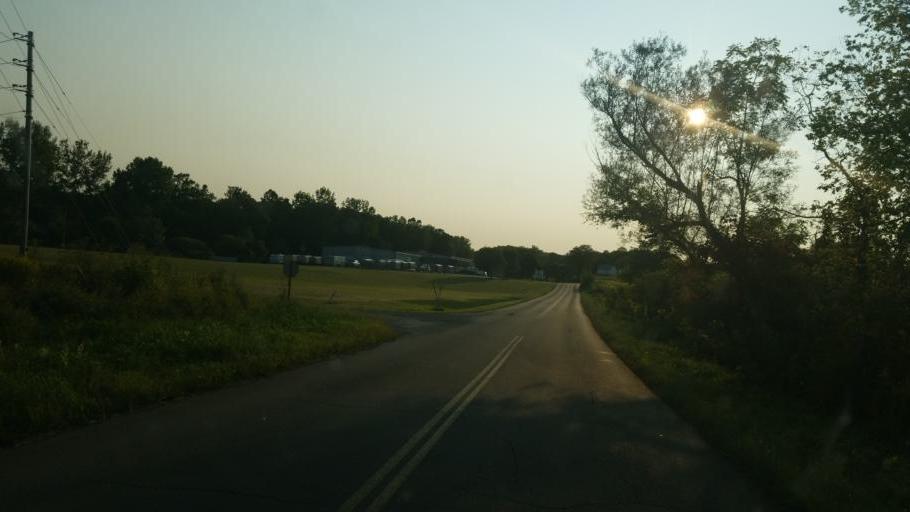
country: US
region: Ohio
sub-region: Wayne County
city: Shreve
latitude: 40.6628
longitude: -81.9611
